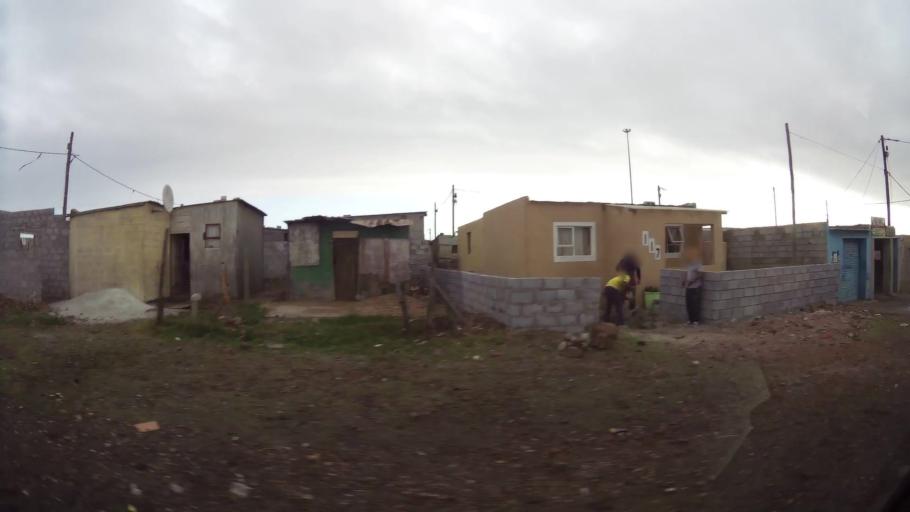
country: ZA
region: Eastern Cape
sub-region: Nelson Mandela Bay Metropolitan Municipality
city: Port Elizabeth
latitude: -33.9102
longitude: 25.5393
